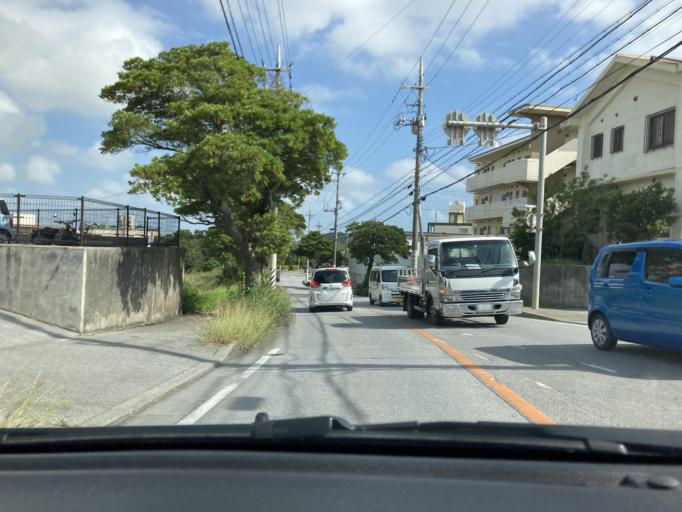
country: JP
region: Okinawa
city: Ginowan
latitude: 26.2549
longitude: 127.7746
